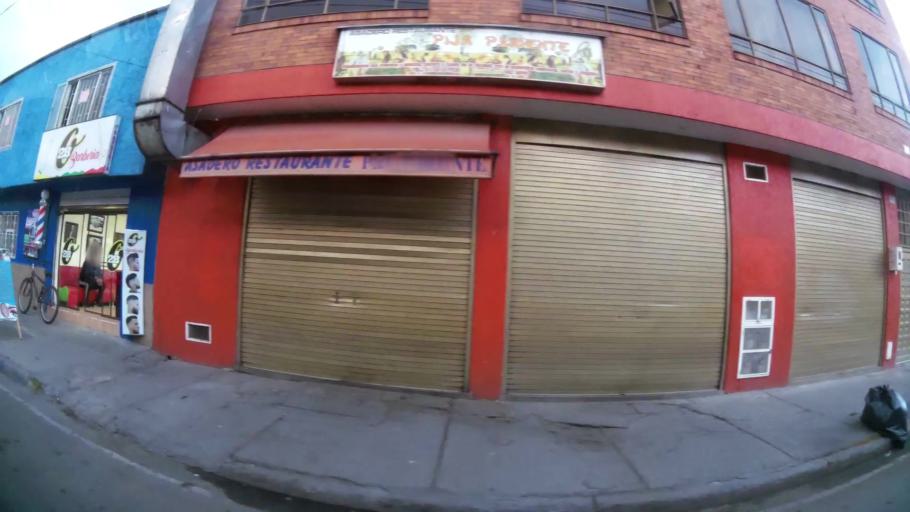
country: CO
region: Bogota D.C.
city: Bogota
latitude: 4.5836
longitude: -74.1383
